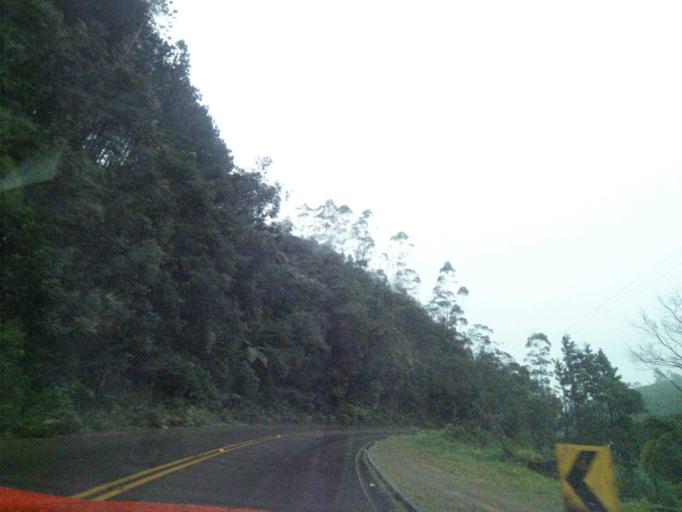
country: BR
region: Santa Catarina
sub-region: Anitapolis
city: Anitapolis
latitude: -27.8370
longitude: -49.0518
